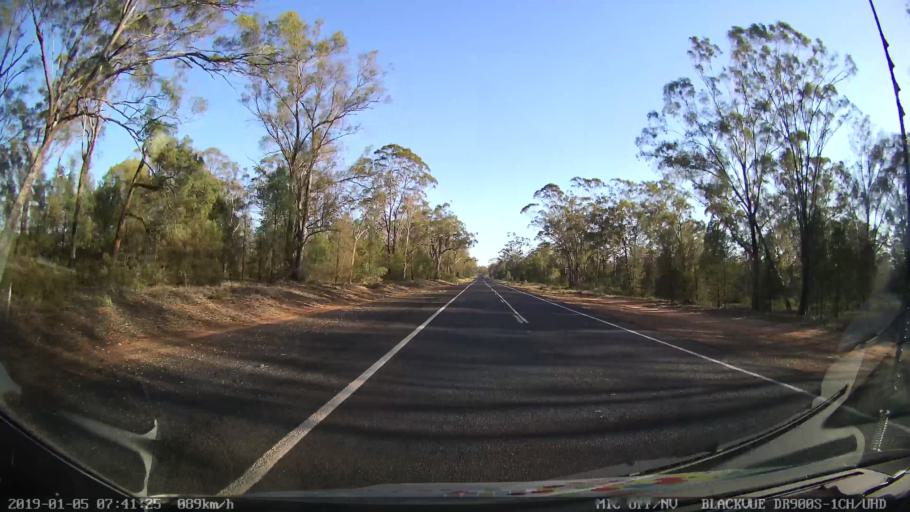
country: AU
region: New South Wales
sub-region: Gilgandra
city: Gilgandra
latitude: -31.9110
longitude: 148.6210
